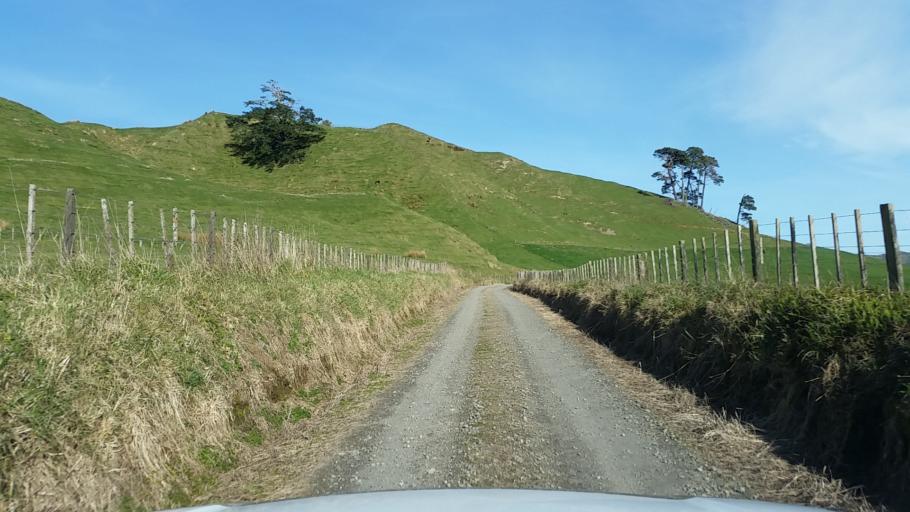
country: NZ
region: Taranaki
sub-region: South Taranaki District
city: Eltham
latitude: -39.3112
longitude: 174.5492
